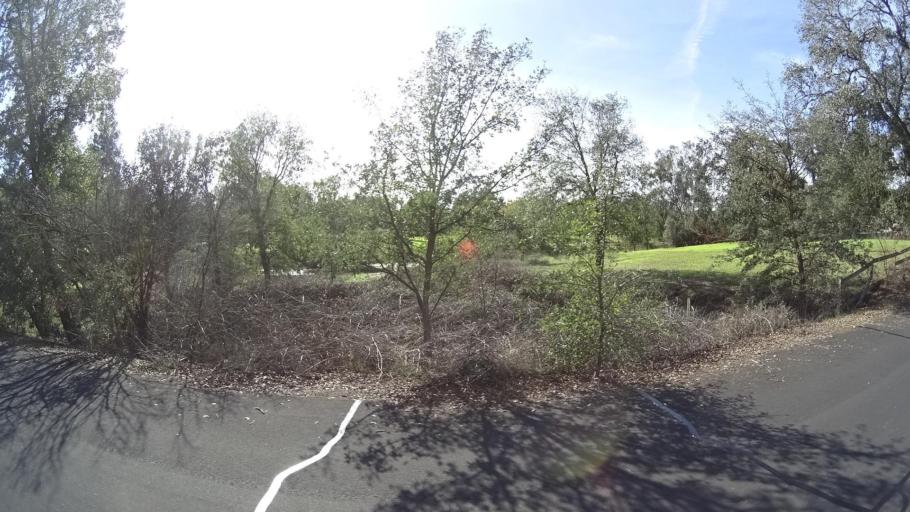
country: US
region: California
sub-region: Sacramento County
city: Wilton
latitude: 38.4327
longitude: -121.2928
